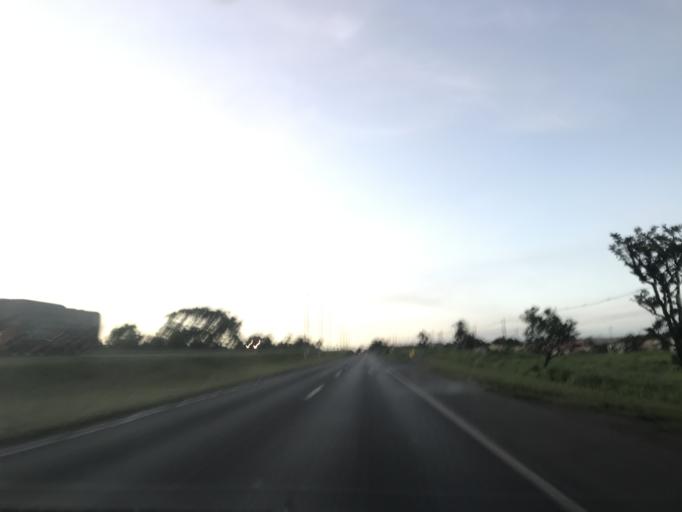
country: BR
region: Goias
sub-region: Luziania
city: Luziania
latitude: -16.1818
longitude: -47.9290
